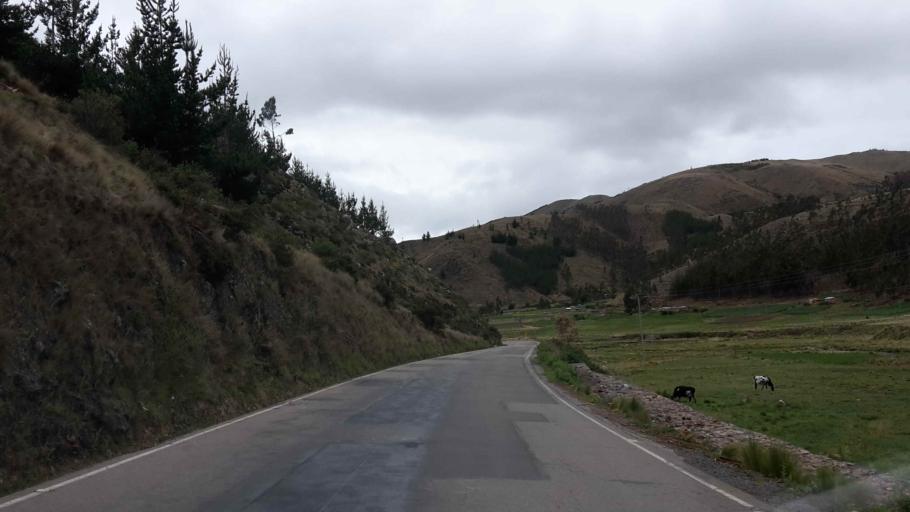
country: BO
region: Cochabamba
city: Arani
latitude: -17.4850
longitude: -65.5523
